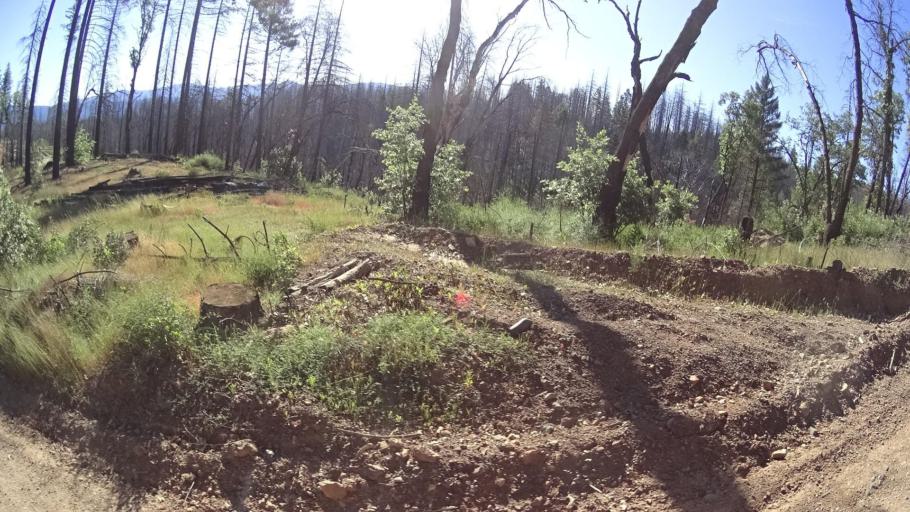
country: US
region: California
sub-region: Lake County
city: Upper Lake
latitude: 39.3904
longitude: -122.9784
